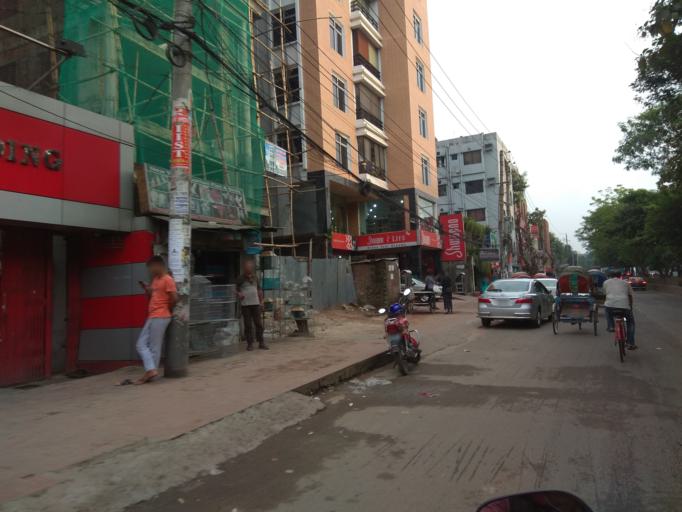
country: BD
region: Dhaka
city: Azimpur
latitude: 23.7610
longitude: 90.3837
